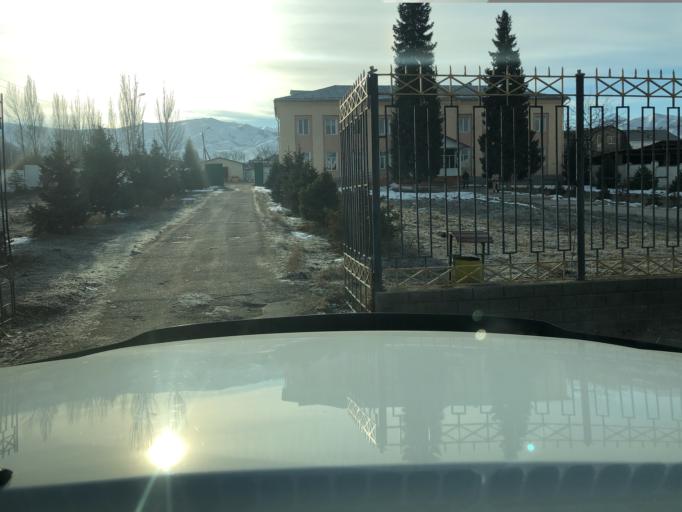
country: KG
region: Ysyk-Koel
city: Pokrovka
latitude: 42.3412
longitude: 78.0029
